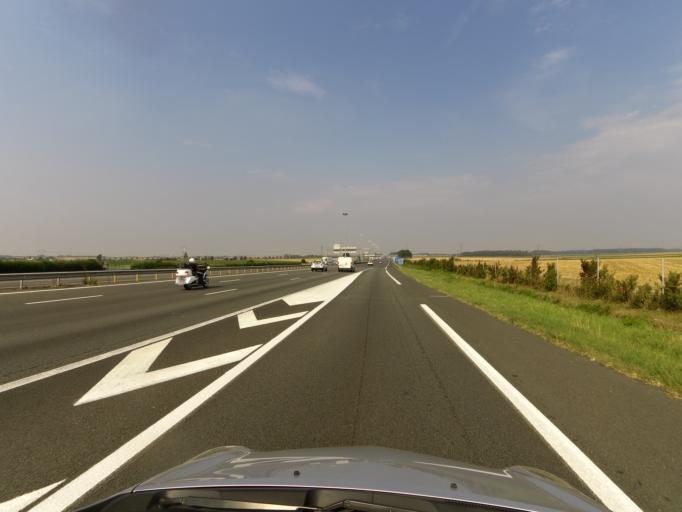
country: FR
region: Nord-Pas-de-Calais
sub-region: Departement du Pas-de-Calais
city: Roeux
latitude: 50.3182
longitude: 2.9043
